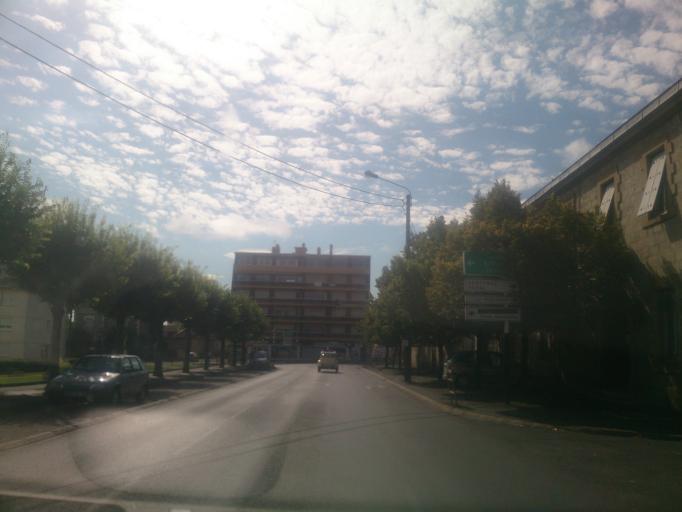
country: FR
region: Limousin
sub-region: Departement de la Correze
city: Brive-la-Gaillarde
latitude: 45.1678
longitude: 1.5327
